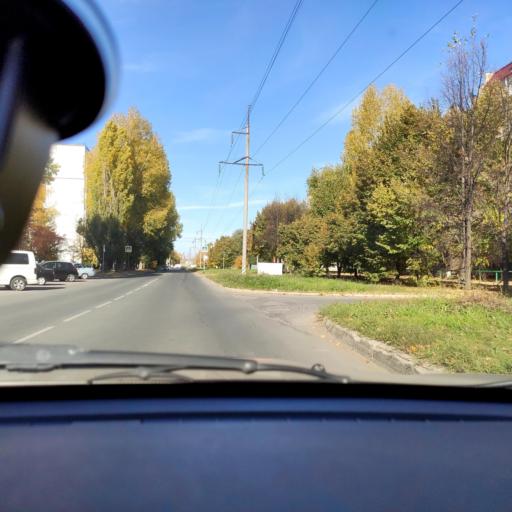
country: RU
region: Samara
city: Tol'yatti
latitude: 53.5084
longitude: 49.4435
